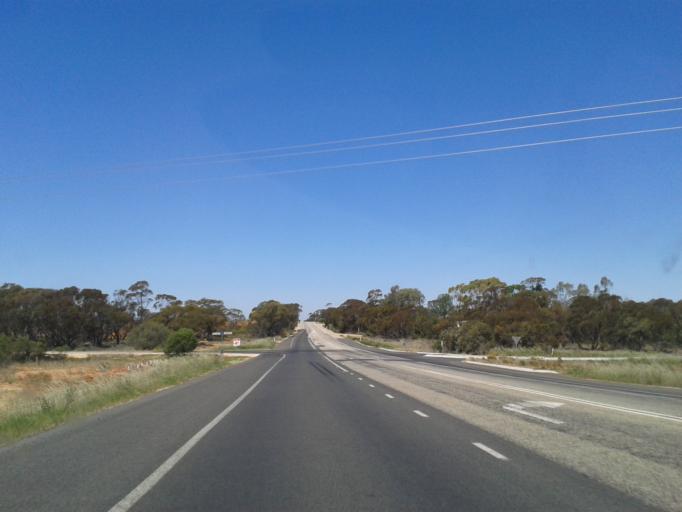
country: AU
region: Victoria
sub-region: Mildura Shire
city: Ouyen
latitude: -34.6215
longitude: 142.8049
